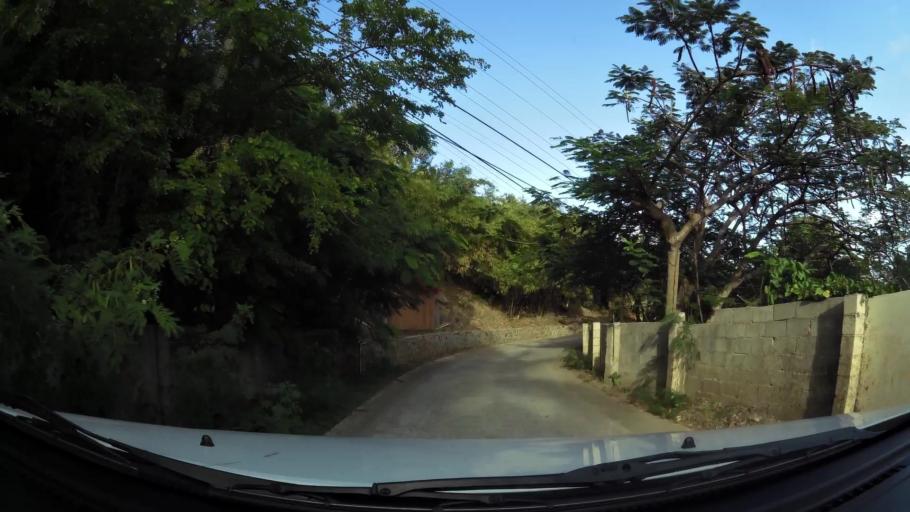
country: LC
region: Gros-Islet
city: Gros Islet
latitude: 14.1040
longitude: -60.9384
